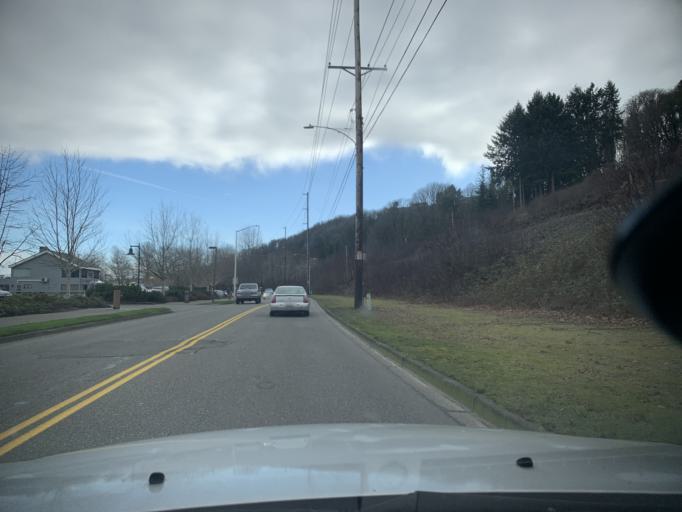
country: US
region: Washington
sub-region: Pierce County
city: Fircrest
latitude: 47.2882
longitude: -122.4905
